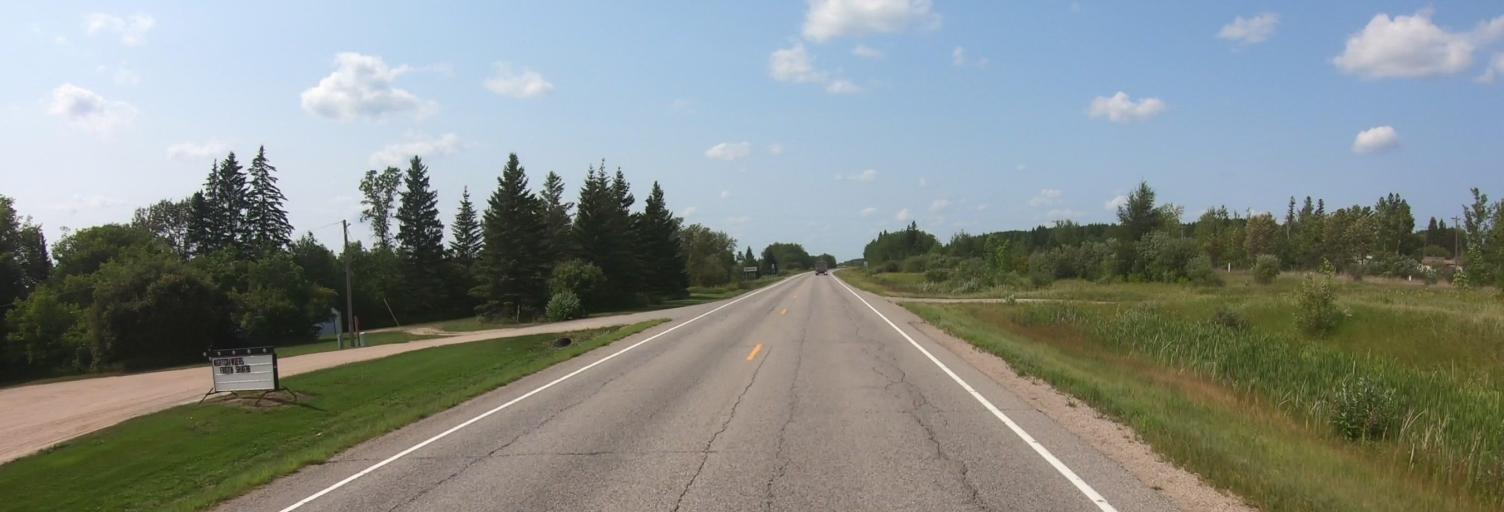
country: US
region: Minnesota
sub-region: Roseau County
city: Warroad
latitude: 48.8031
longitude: -95.1001
